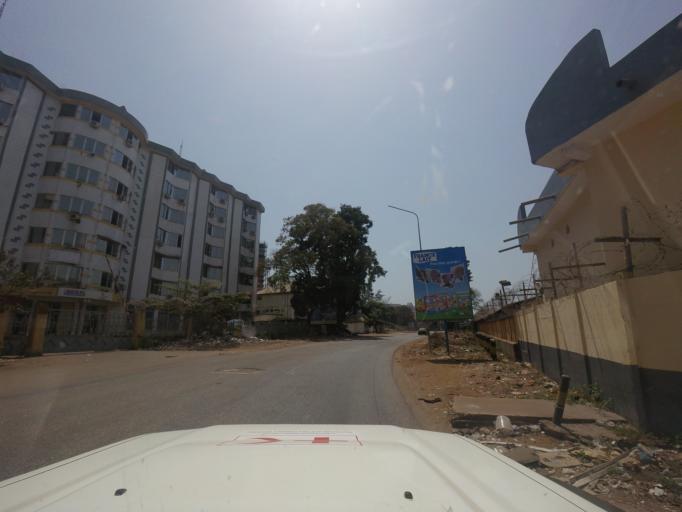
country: GN
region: Conakry
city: Camayenne
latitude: 9.5154
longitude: -13.7076
